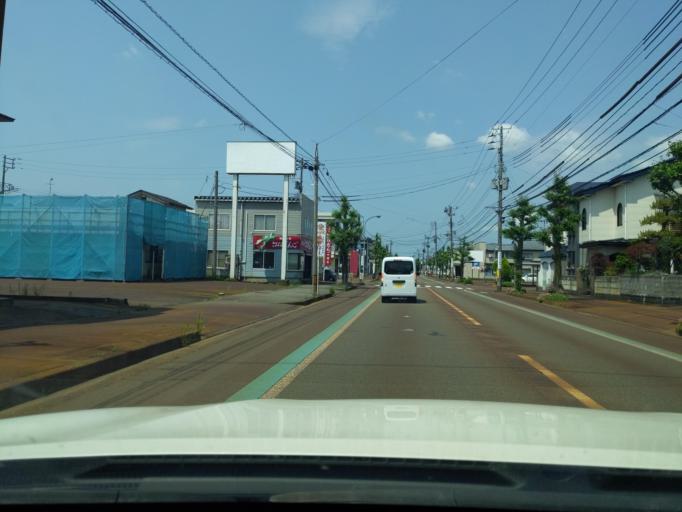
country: JP
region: Niigata
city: Nagaoka
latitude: 37.4294
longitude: 138.8512
